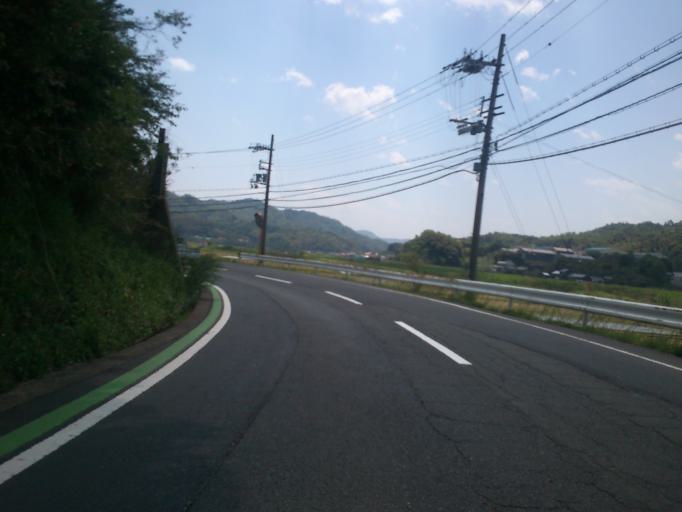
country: JP
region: Kyoto
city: Miyazu
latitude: 35.7267
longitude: 135.1038
